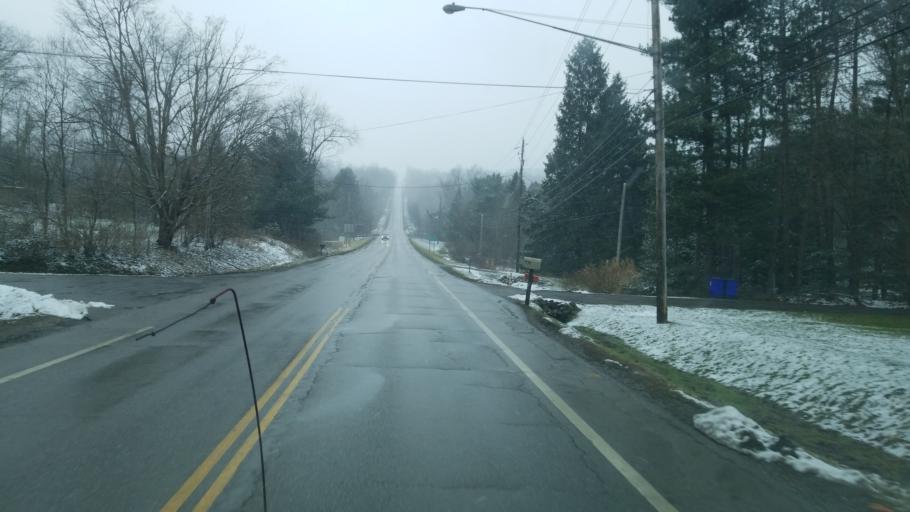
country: US
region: Ohio
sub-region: Portage County
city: Mantua
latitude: 41.3105
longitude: -81.1915
